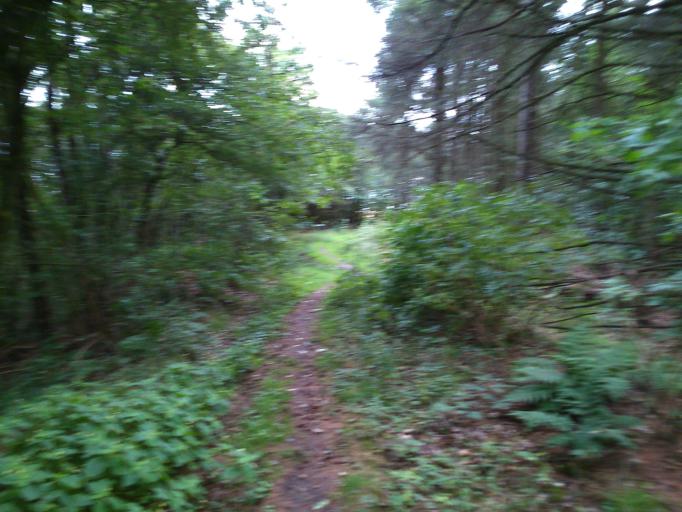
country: DK
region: Central Jutland
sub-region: Ringkobing-Skjern Kommune
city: Videbaek
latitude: 56.0136
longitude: 8.6325
